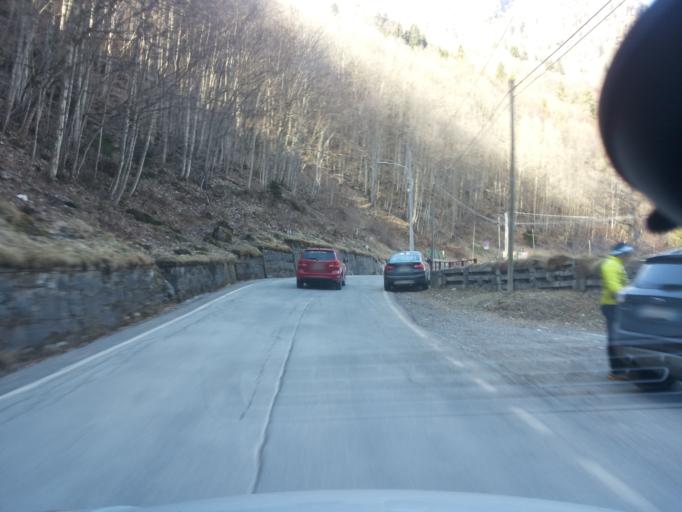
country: IT
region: Piedmont
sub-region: Provincia di Vercelli
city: Alagna Valsesia
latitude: 45.8593
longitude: 7.9363
